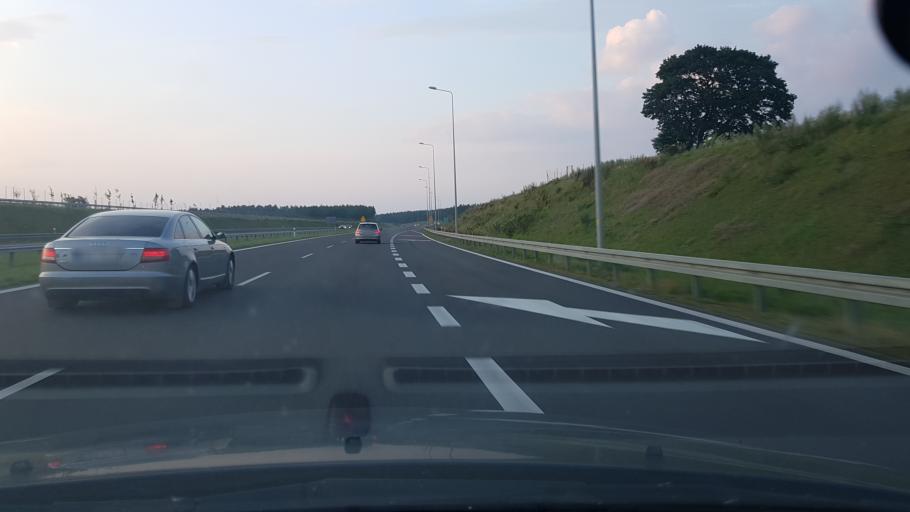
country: PL
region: Masovian Voivodeship
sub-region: Powiat mlawski
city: Wieczfnia Koscielna
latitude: 53.2316
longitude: 20.4196
